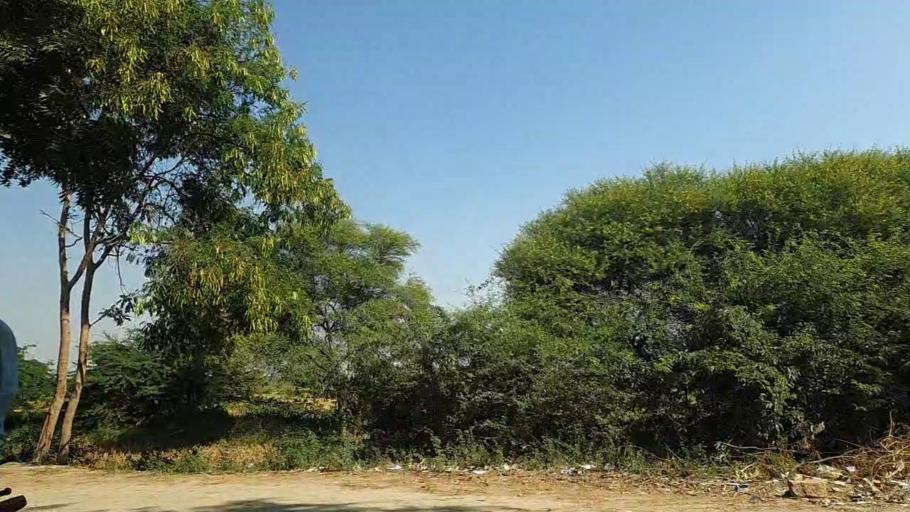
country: PK
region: Sindh
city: Daro Mehar
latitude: 24.7255
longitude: 68.1808
